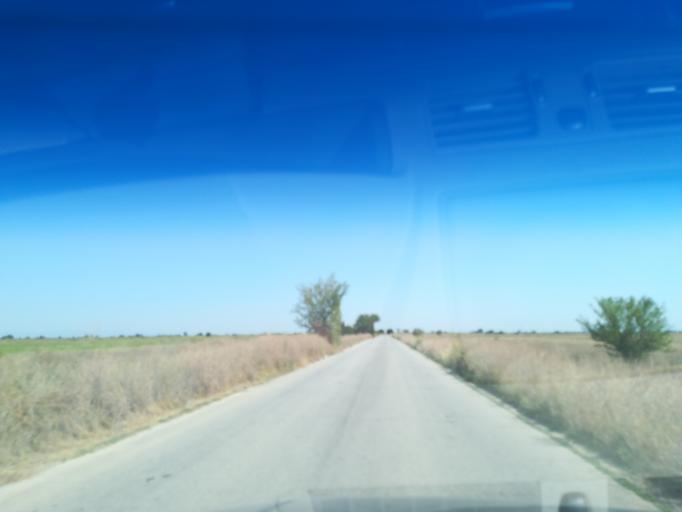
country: BG
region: Plovdiv
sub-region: Obshtina Suedinenie
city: Suedinenie
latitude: 42.2516
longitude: 24.4591
